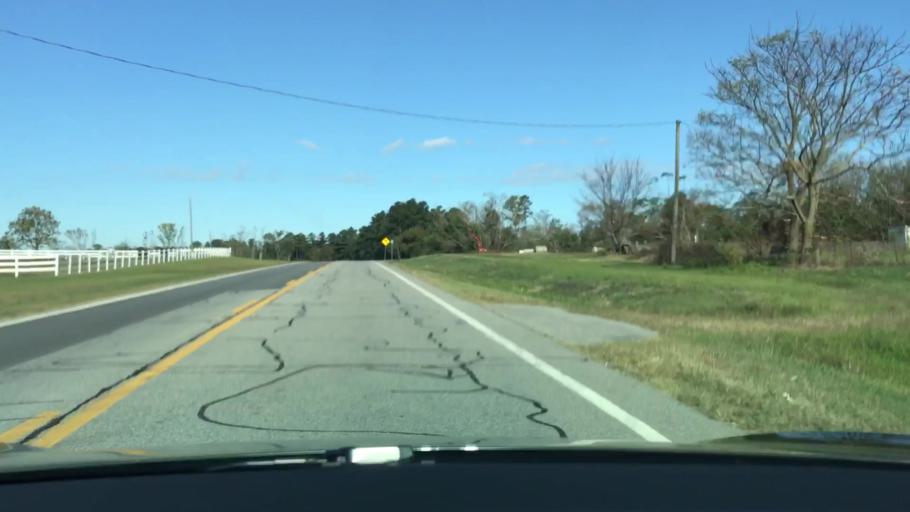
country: US
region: Georgia
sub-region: Warren County
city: Warrenton
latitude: 33.3702
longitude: -82.6011
